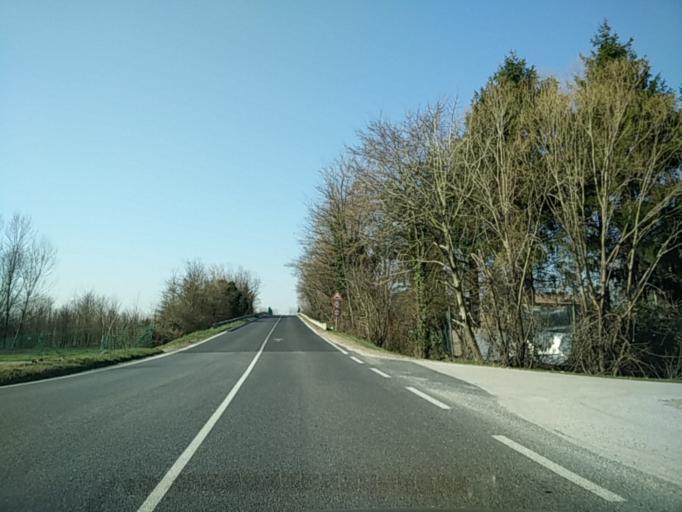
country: IT
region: Friuli Venezia Giulia
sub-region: Provincia di Pordenone
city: Villotta
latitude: 45.8610
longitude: 12.7748
